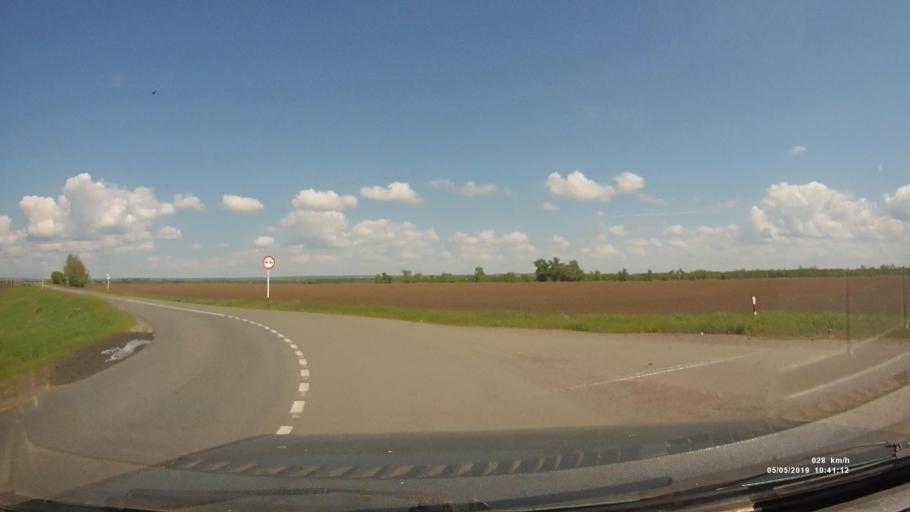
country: RU
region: Rostov
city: Ust'-Donetskiy
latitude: 47.5893
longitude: 40.8434
